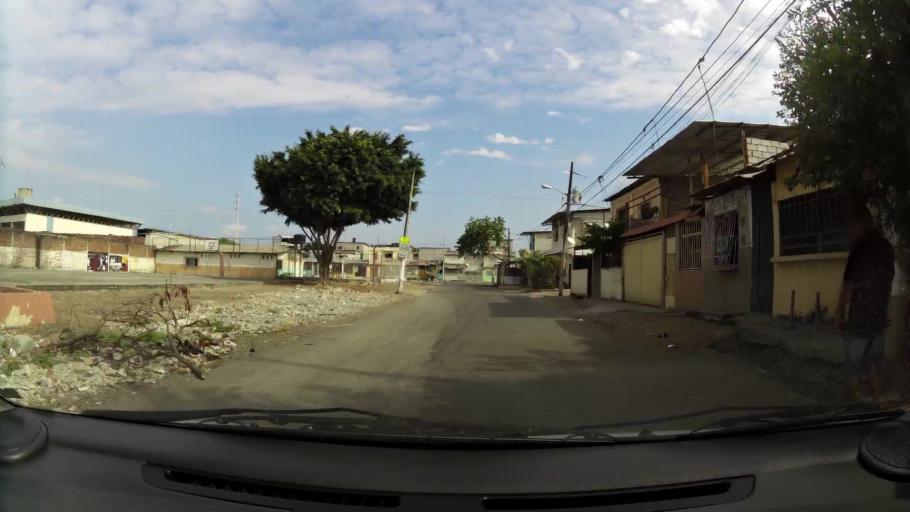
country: EC
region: Guayas
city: Guayaquil
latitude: -2.2581
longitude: -79.8772
